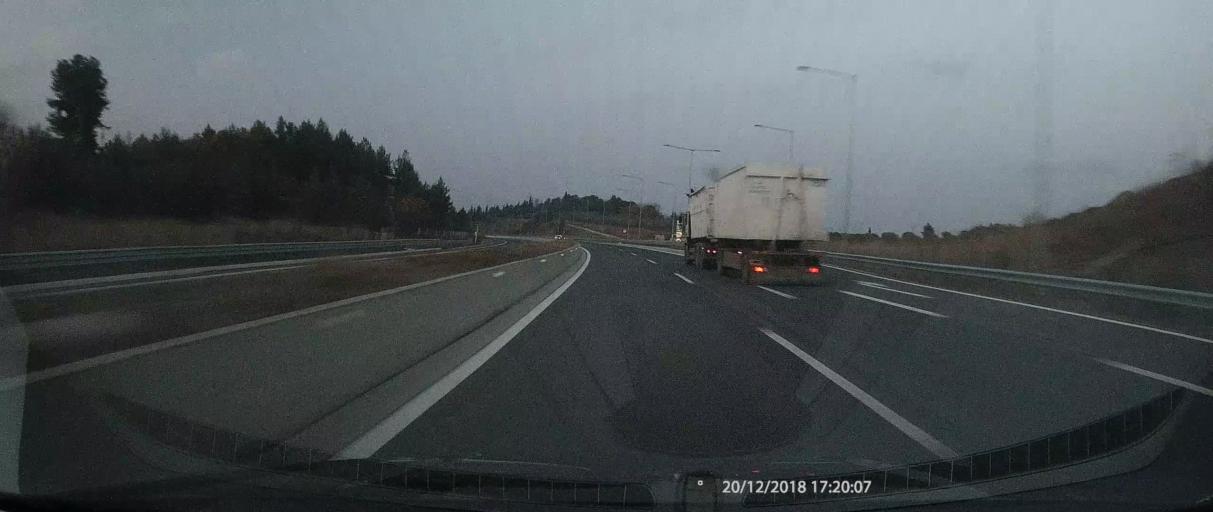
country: GR
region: Thessaly
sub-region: Nomos Larisis
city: Pyrgetos
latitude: 39.9588
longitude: 22.6469
